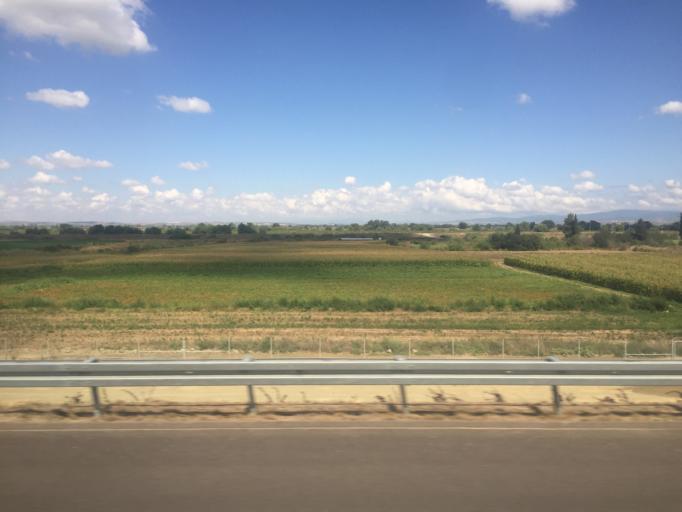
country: TR
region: Bursa
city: Karacabey
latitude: 40.1347
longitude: 28.2949
